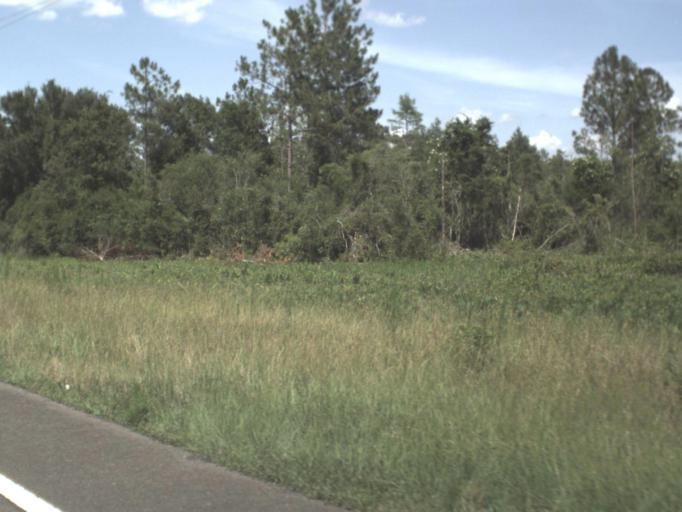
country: US
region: Florida
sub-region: Gilchrist County
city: Trenton
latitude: 29.6948
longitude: -82.7615
